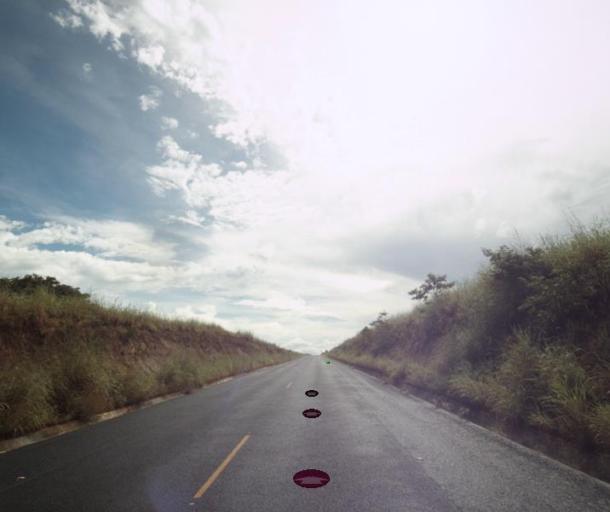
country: BR
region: Goias
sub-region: Sao Miguel Do Araguaia
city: Sao Miguel do Araguaia
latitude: -13.2966
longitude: -50.3479
